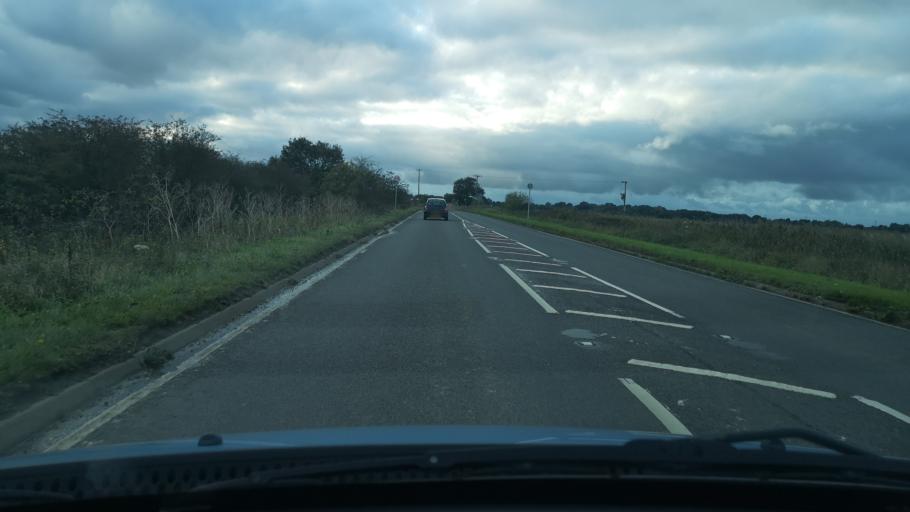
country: GB
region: England
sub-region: North Lincolnshire
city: Belton
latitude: 53.5806
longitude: -0.7889
